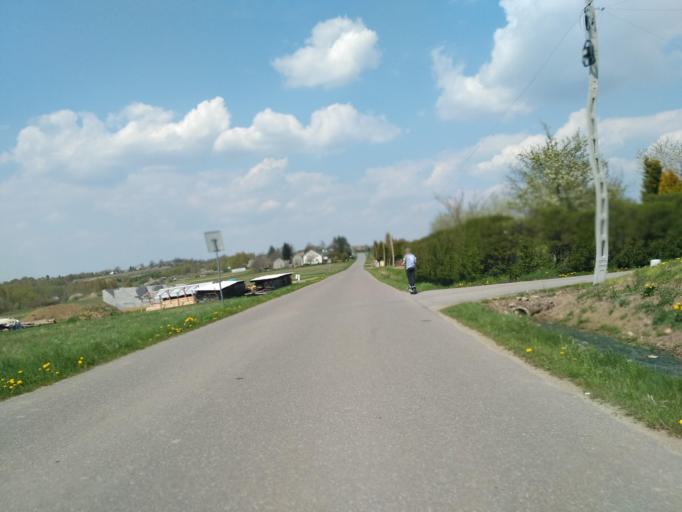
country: PL
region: Subcarpathian Voivodeship
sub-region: Powiat jasielski
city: Debowiec
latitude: 49.6908
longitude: 21.5158
